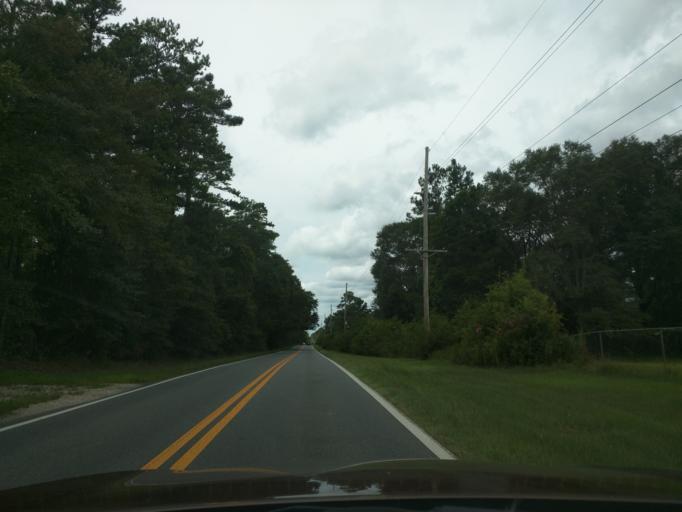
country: US
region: Florida
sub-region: Leon County
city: Tallahassee
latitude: 30.5364
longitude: -84.1347
